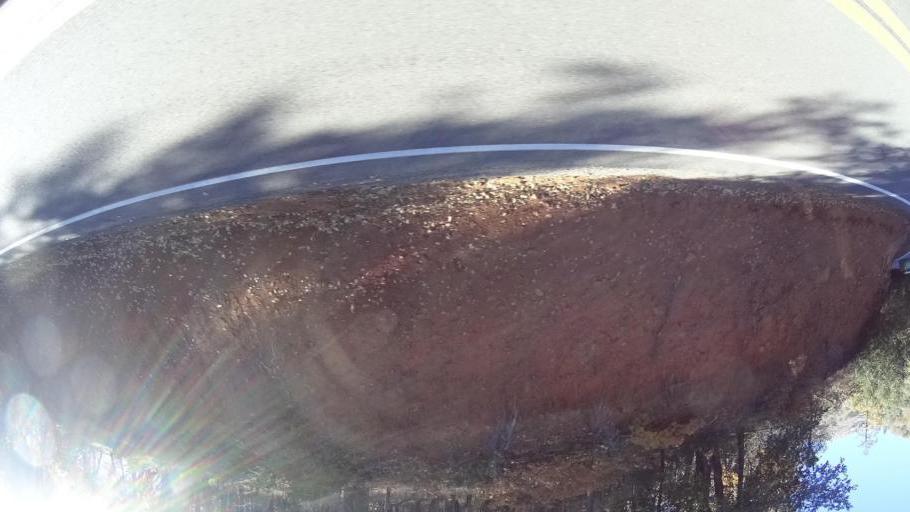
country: US
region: California
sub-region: Kern County
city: Alta Sierra
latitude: 35.7479
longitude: -118.5838
